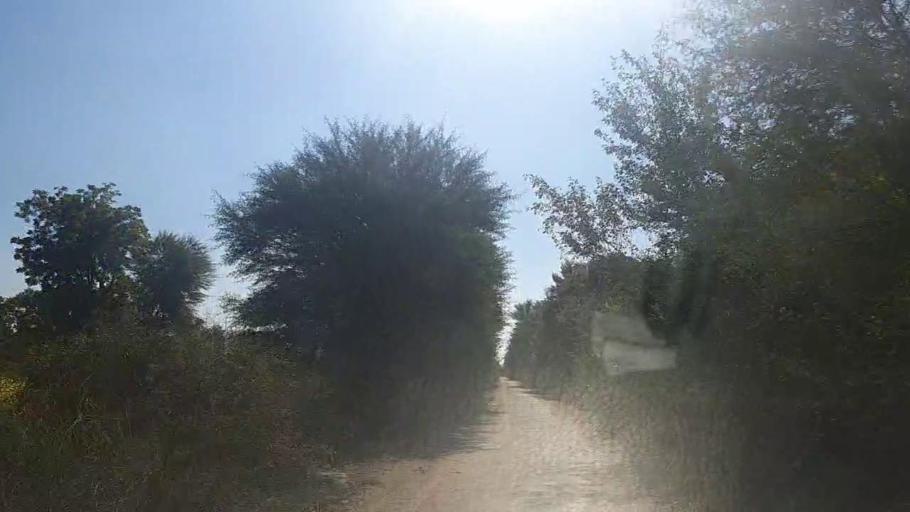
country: PK
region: Sindh
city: Khadro
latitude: 26.1502
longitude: 68.8379
